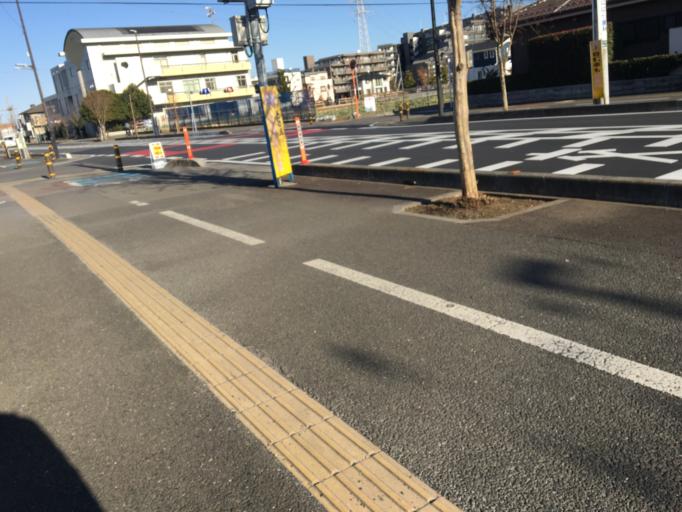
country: JP
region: Saitama
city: Oi
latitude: 35.8417
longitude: 139.5339
